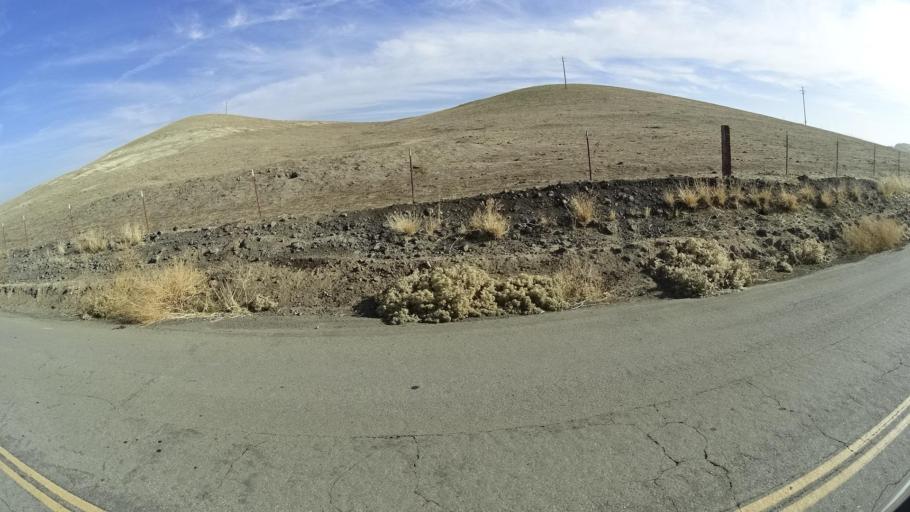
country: US
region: California
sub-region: Kern County
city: Oildale
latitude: 35.6177
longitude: -118.9866
